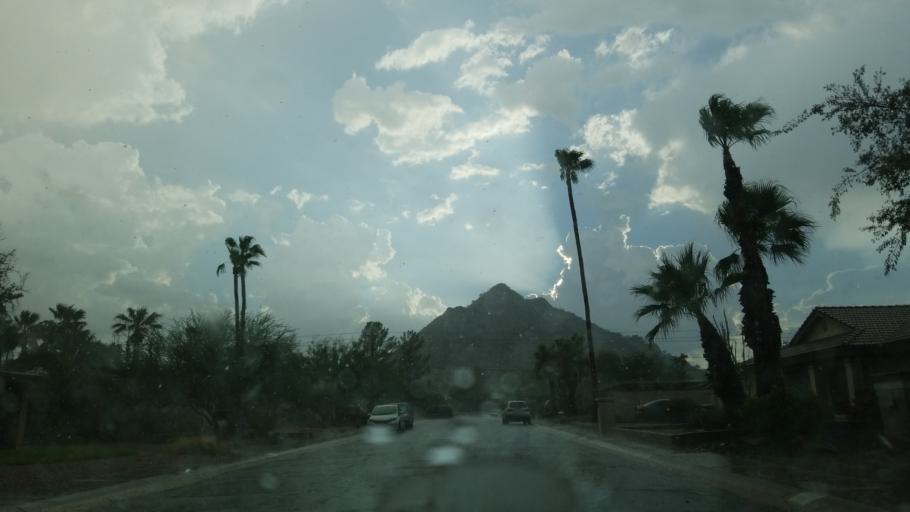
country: US
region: Arizona
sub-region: Maricopa County
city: Paradise Valley
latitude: 33.5888
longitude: -112.0291
